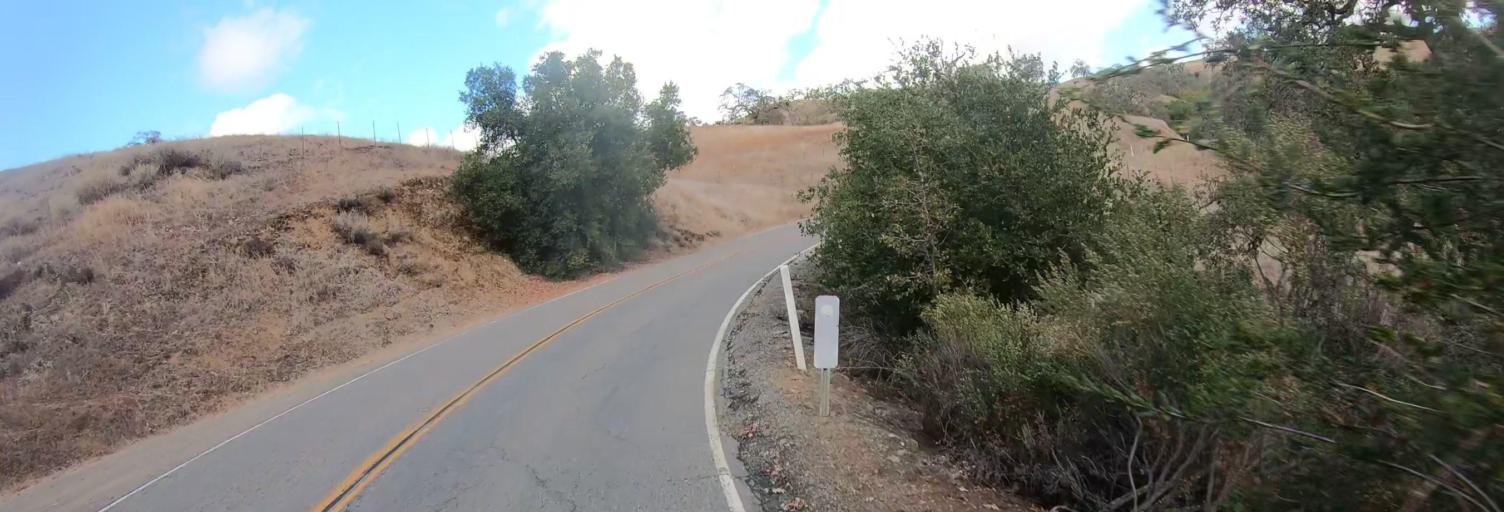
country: US
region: California
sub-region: Santa Clara County
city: East Foothills
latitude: 37.3304
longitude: -121.6896
